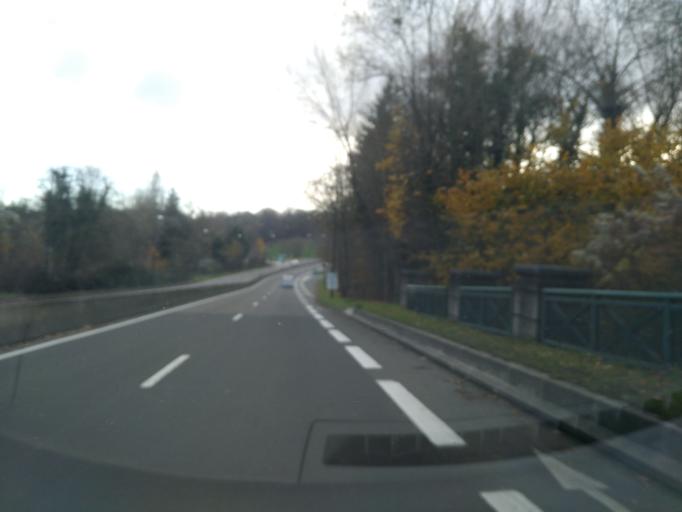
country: FR
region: Ile-de-France
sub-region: Departement des Yvelines
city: Guyancourt
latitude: 48.7805
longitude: 2.0957
